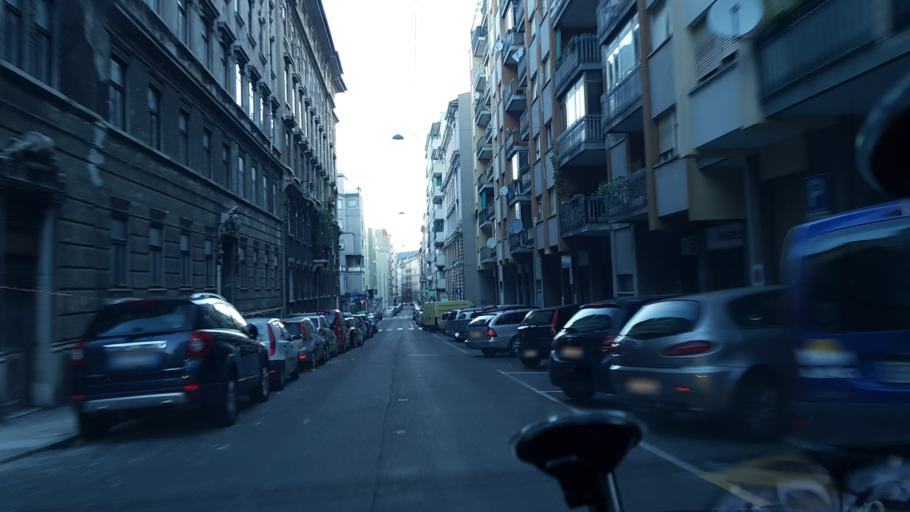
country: IT
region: Friuli Venezia Giulia
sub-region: Provincia di Trieste
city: Trieste
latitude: 45.6456
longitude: 13.7881
